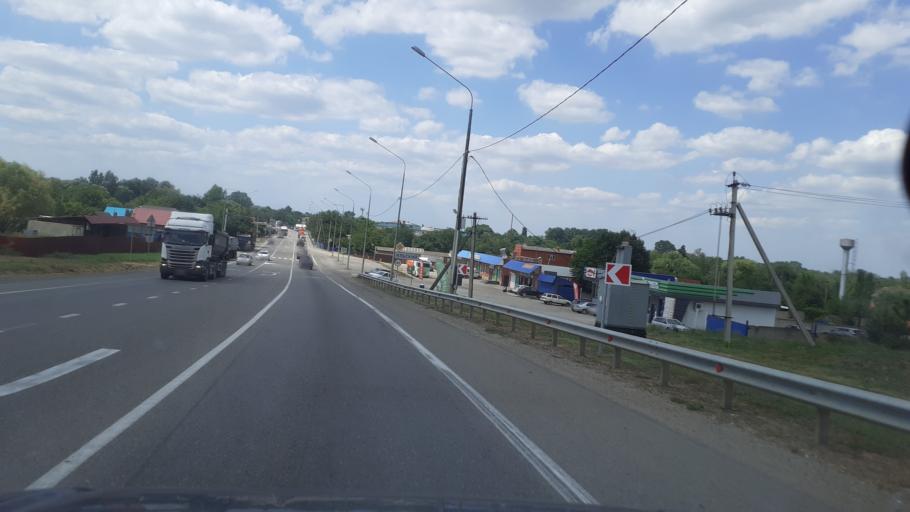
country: RU
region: Krasnodarskiy
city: Il'skiy
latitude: 44.8528
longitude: 38.5929
